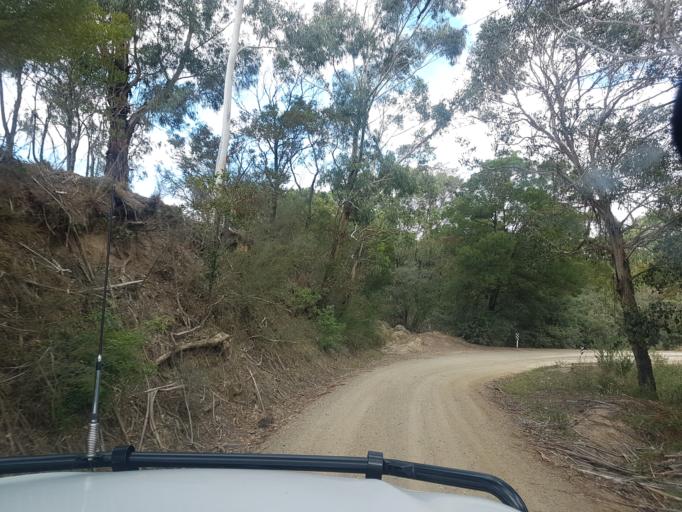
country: AU
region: Victoria
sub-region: East Gippsland
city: Bairnsdale
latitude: -37.7842
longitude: 147.5489
